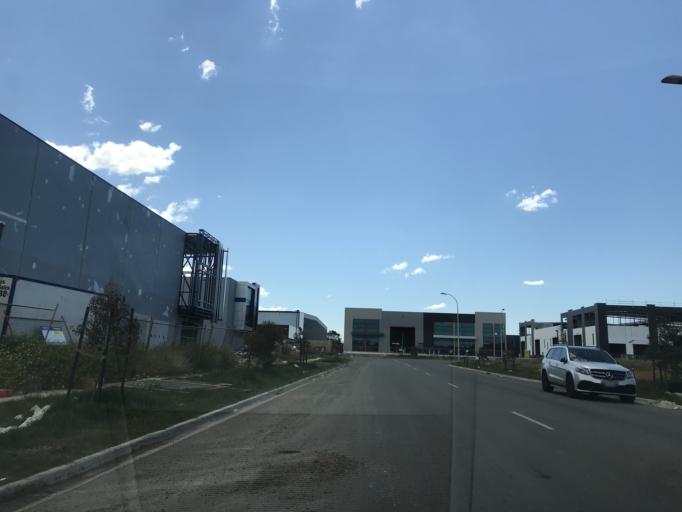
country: AU
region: Victoria
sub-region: Wyndham
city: Truganina
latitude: -37.8368
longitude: 144.7455
